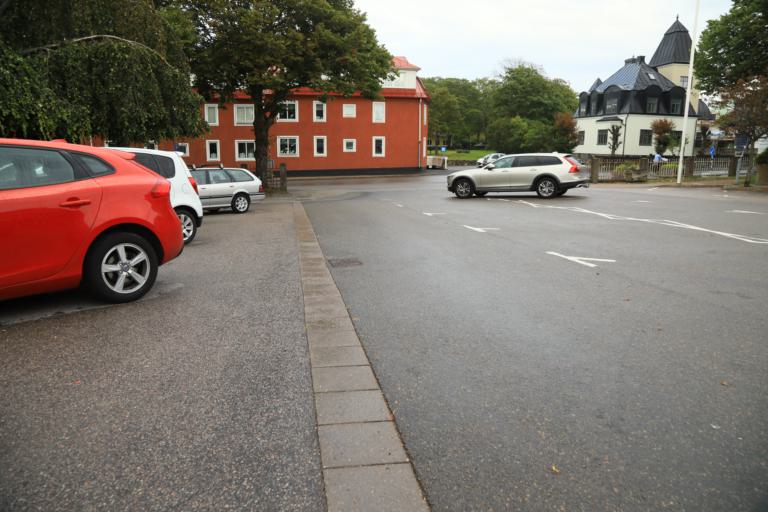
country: SE
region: Halland
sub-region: Varbergs Kommun
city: Varberg
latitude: 57.1037
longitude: 12.2475
